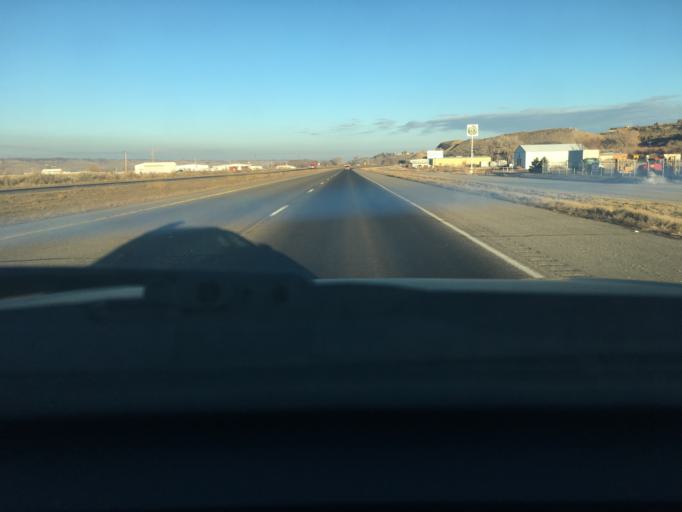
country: US
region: Colorado
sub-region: Montrose County
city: Montrose
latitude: 38.5271
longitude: -107.9317
